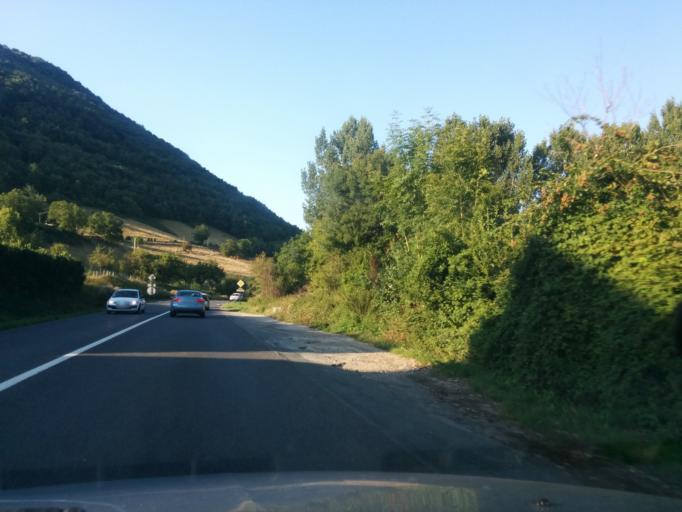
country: FR
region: Rhone-Alpes
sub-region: Departement de l'Isere
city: Chirens
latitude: 45.4178
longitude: 5.5519
